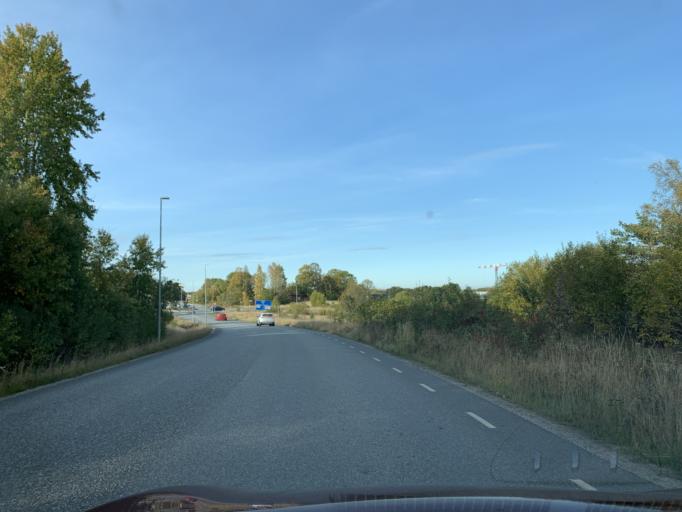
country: SE
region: Stockholm
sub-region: Upplands-Bro Kommun
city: Bro
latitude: 59.5115
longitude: 17.6161
